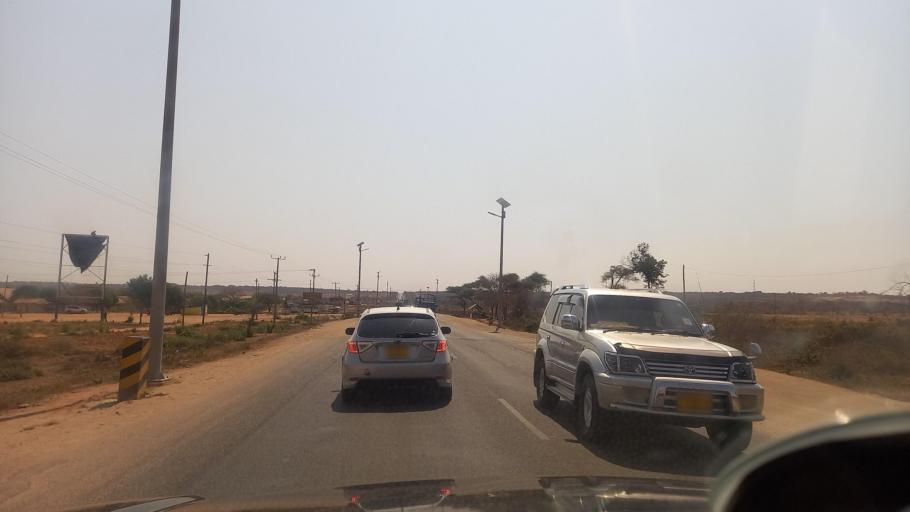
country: TZ
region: Dodoma
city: Kisasa
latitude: -6.1456
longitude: 35.8286
